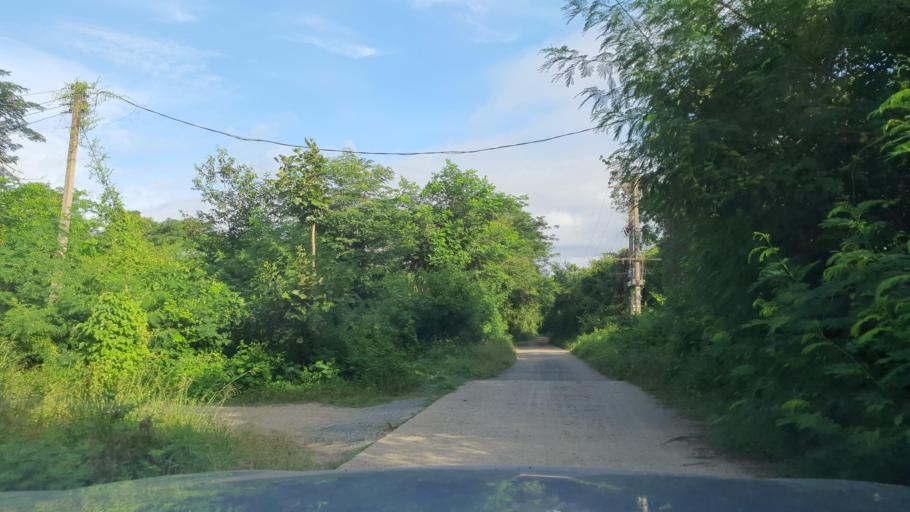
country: TH
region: Chiang Mai
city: San Kamphaeng
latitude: 18.7499
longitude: 99.1022
